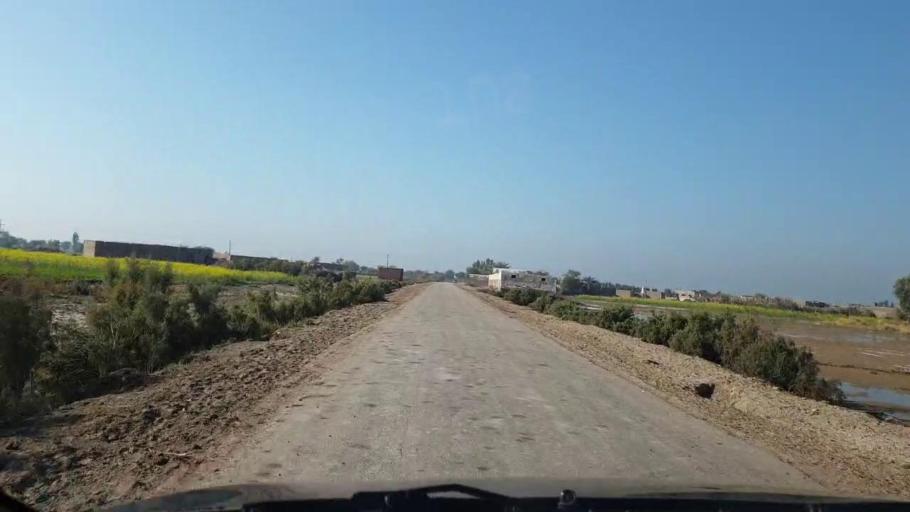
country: PK
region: Sindh
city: Sinjhoro
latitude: 26.0144
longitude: 68.7909
